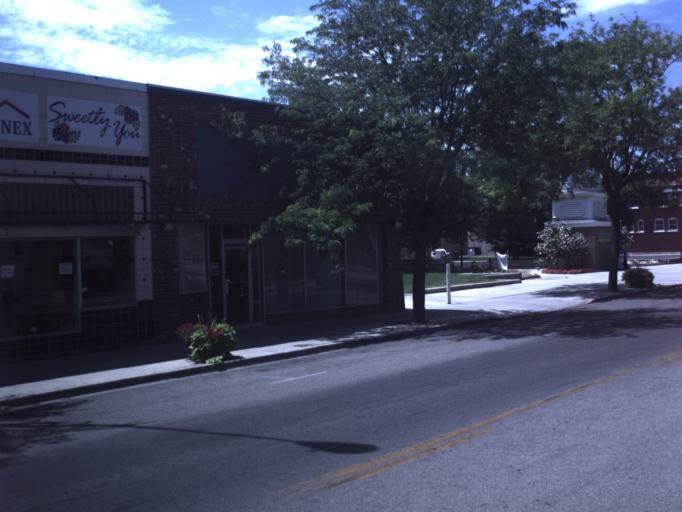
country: US
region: Utah
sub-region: Box Elder County
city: Tremonton
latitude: 41.7118
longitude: -112.1665
